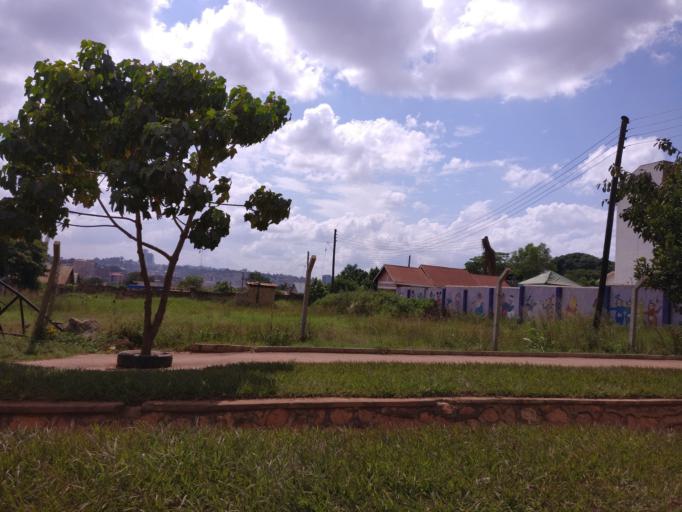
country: UG
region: Central Region
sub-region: Kampala District
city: Kampala
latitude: 0.3055
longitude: 32.5627
